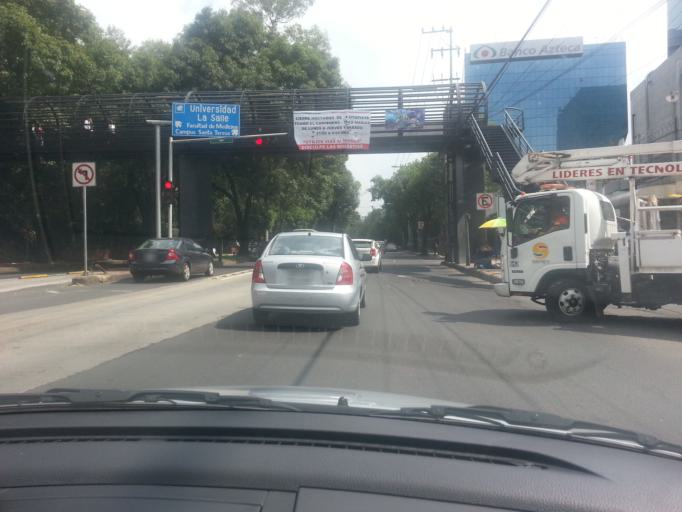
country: MX
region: Mexico City
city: Tlalpan
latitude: 19.2977
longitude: -99.1854
